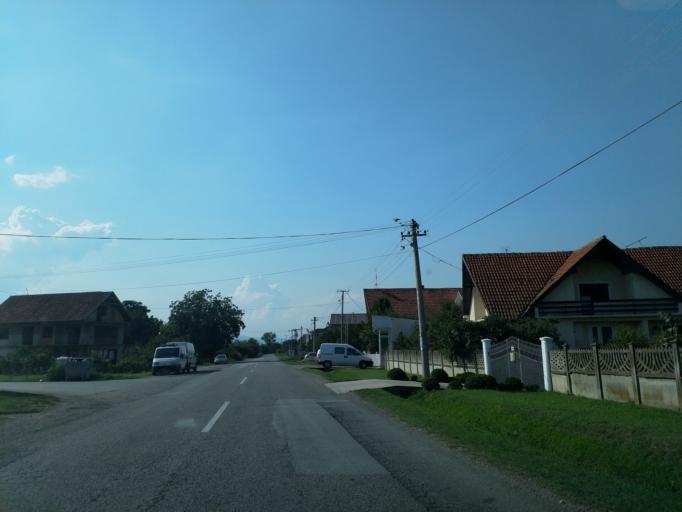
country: RS
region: Central Serbia
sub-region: Rasinski Okrug
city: Cicevac
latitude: 43.7526
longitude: 21.4392
